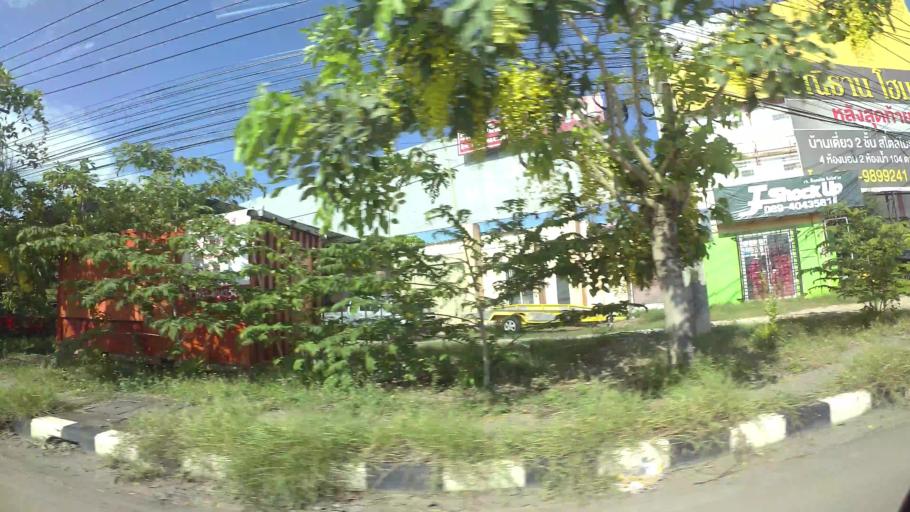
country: TH
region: Rayong
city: Rayong
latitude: 12.6703
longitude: 101.2942
